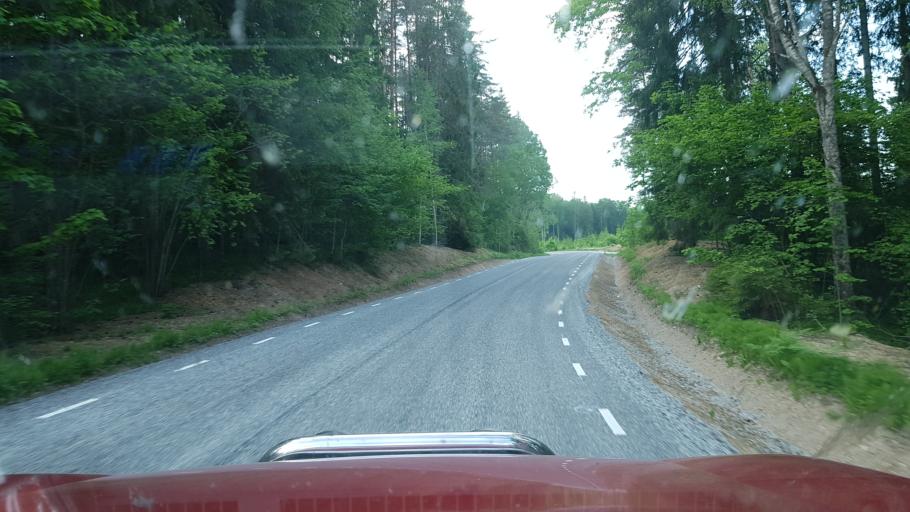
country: EE
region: Tartu
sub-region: UElenurme vald
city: Ulenurme
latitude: 58.0945
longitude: 26.8055
